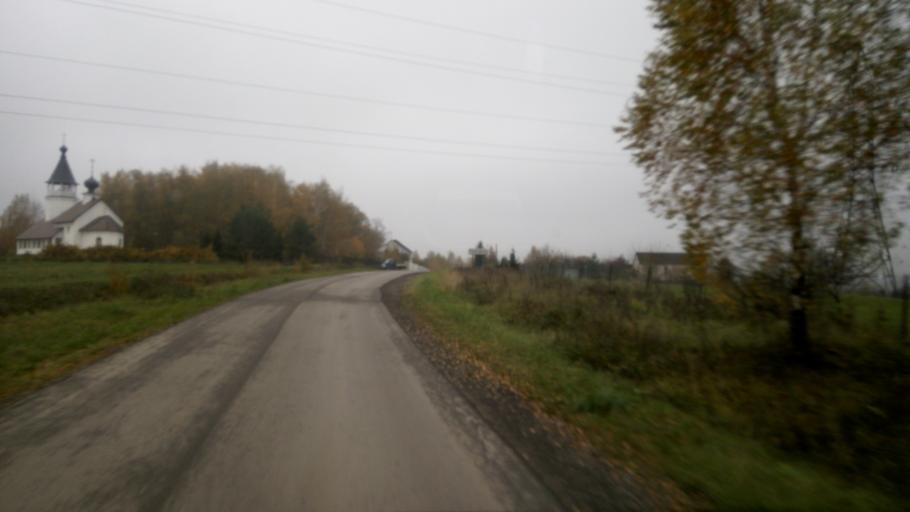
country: RU
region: Moskovskaya
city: Skhodnya
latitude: 55.9265
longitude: 37.2696
